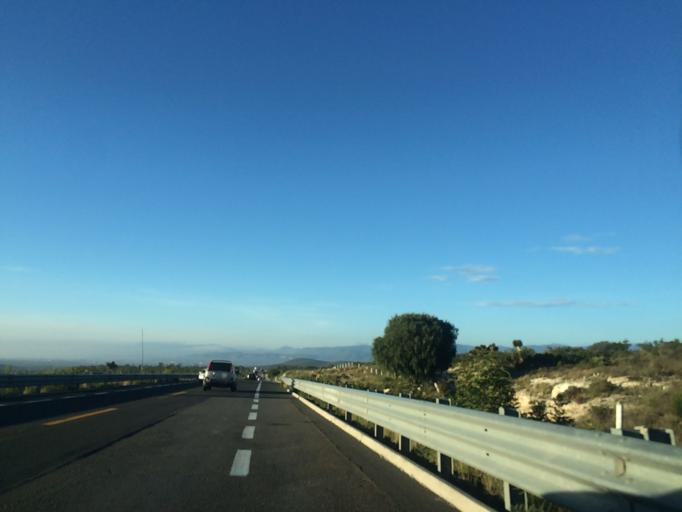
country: MX
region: Puebla
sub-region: Tehuacan
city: Magdalena Cuayucatepec
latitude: 18.6097
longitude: -97.4755
